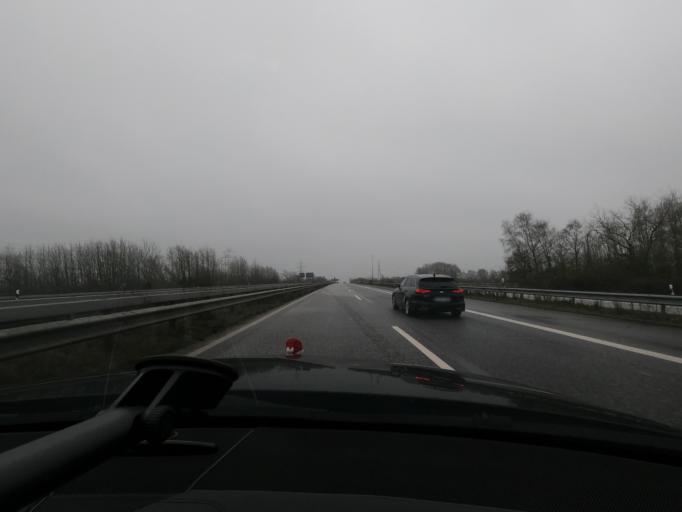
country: DE
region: Schleswig-Holstein
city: Schulldorf
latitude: 54.3042
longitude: 9.7555
